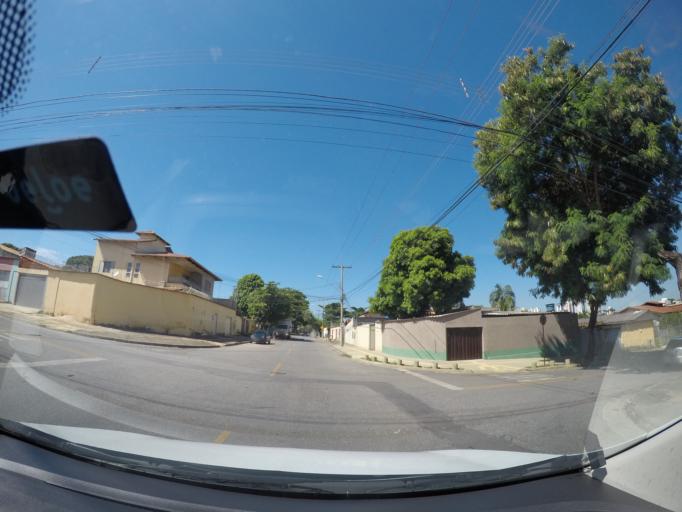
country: BR
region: Goias
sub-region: Goiania
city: Goiania
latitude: -16.6968
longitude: -49.2913
